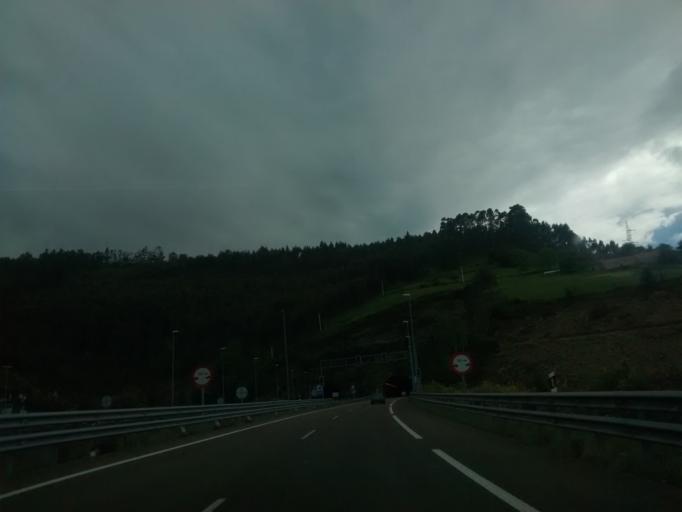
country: ES
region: Asturias
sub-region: Province of Asturias
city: Arriba
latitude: 43.4951
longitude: -5.5332
